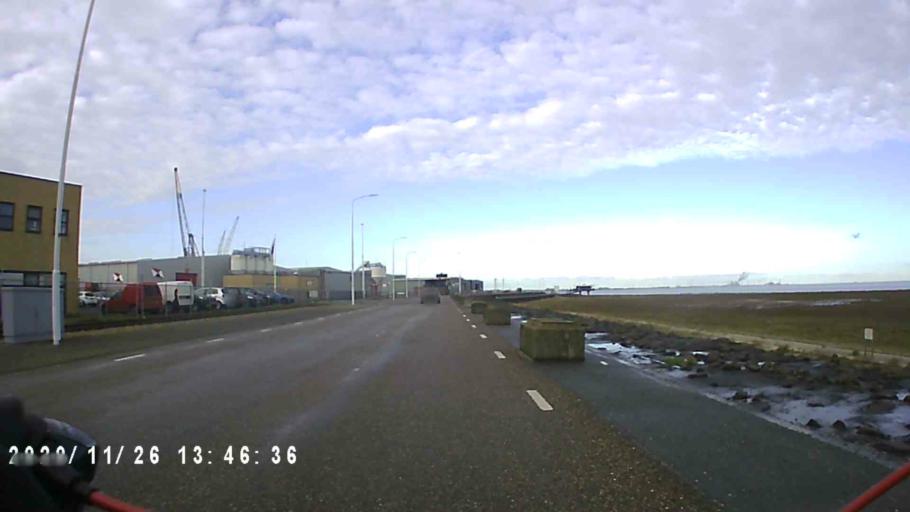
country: NL
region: Groningen
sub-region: Gemeente Delfzijl
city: Delfzijl
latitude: 53.3316
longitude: 6.9396
